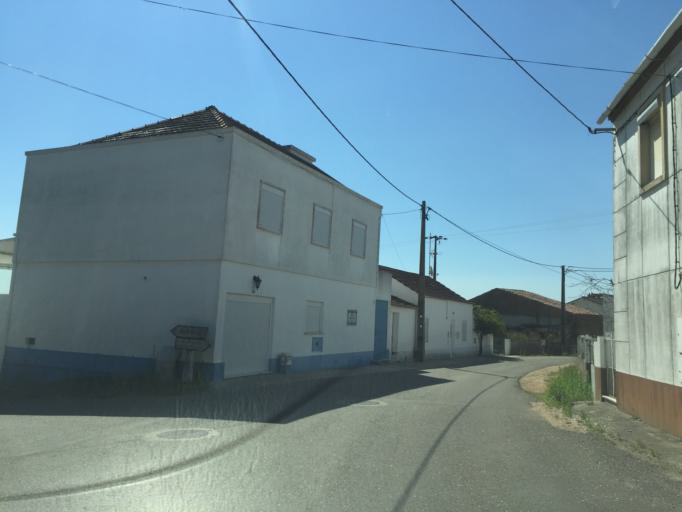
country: PT
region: Santarem
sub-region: Ferreira do Zezere
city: Ferreira do Zezere
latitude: 39.5891
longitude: -8.2793
